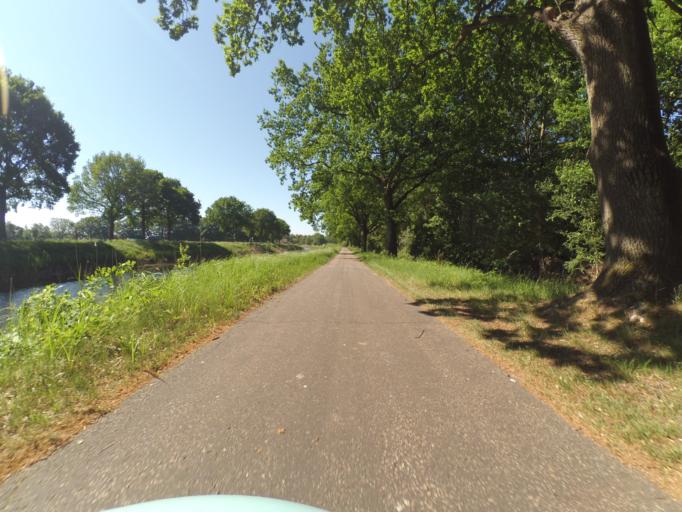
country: NL
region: Gelderland
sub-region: Gemeente Epe
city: Emst
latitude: 52.3025
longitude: 6.0009
